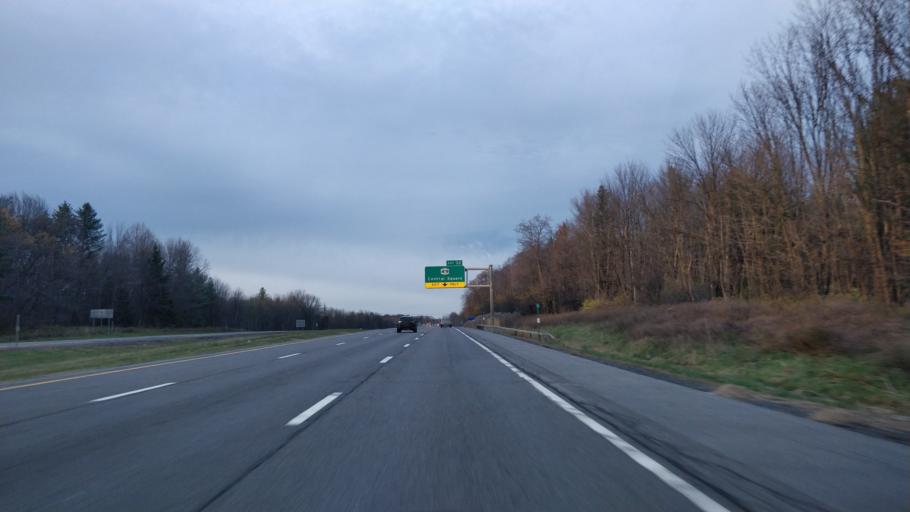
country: US
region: New York
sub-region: Oswego County
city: Central Square
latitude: 43.2731
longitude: -76.1295
